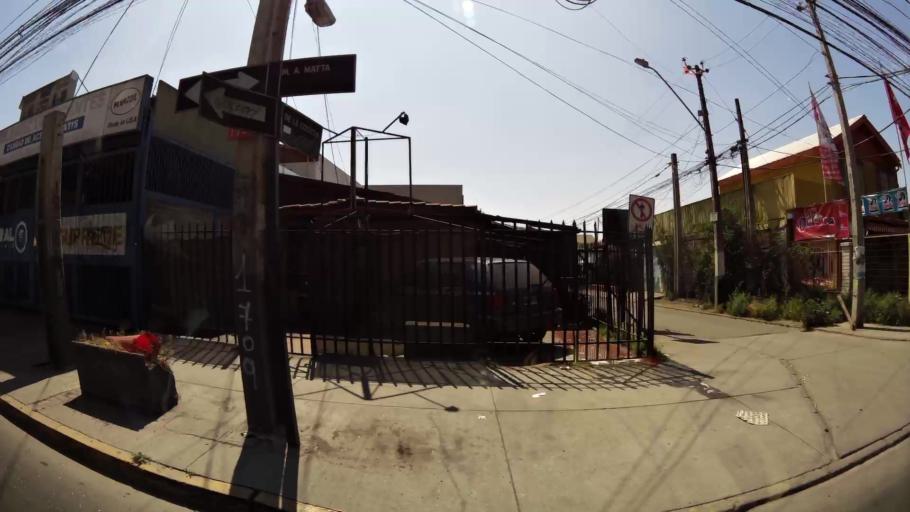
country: CL
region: Santiago Metropolitan
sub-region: Provincia de Santiago
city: Lo Prado
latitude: -33.3656
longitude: -70.7265
